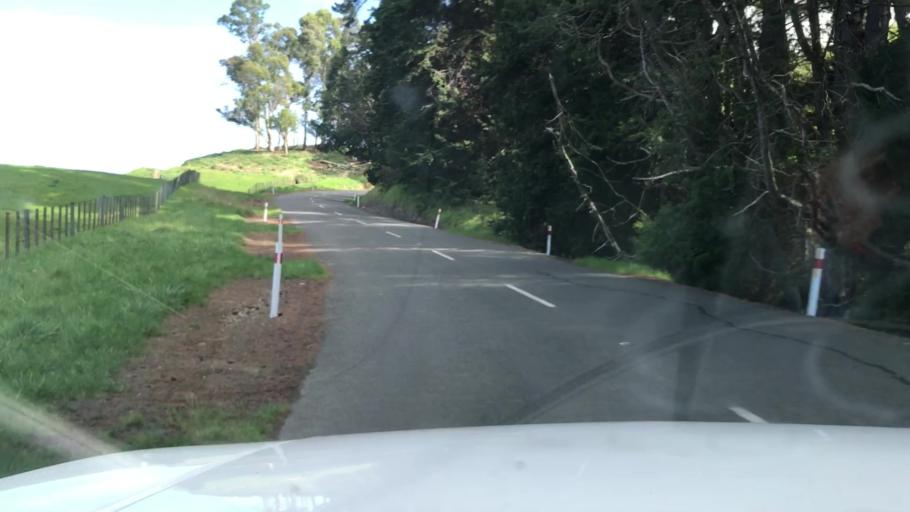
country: NZ
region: Hawke's Bay
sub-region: Hastings District
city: Hastings
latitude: -39.8142
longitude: 176.7520
